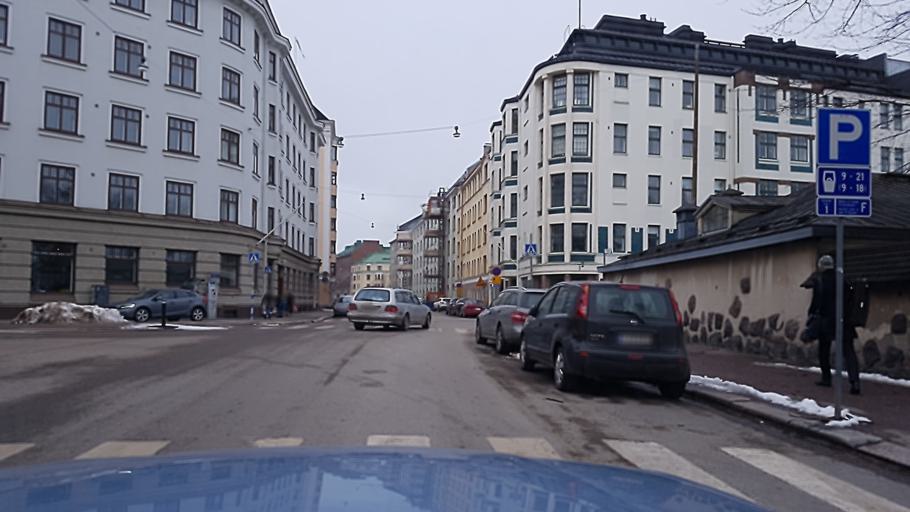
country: FI
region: Uusimaa
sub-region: Helsinki
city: Helsinki
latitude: 60.1756
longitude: 24.9298
